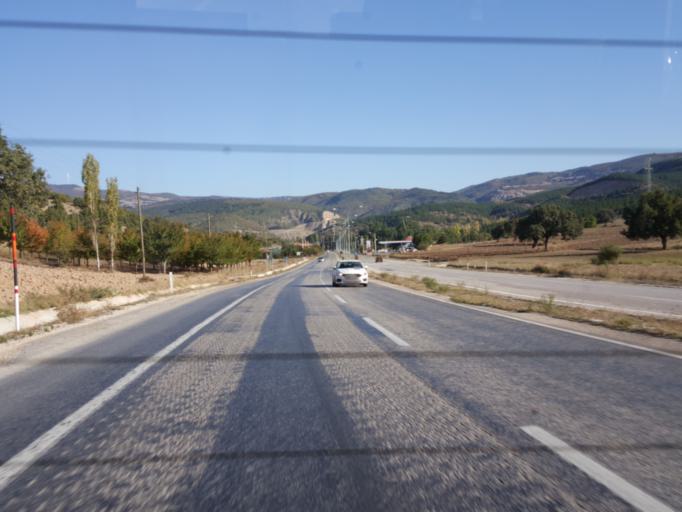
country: TR
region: Amasya
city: Ezinepazari
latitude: 40.5601
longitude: 36.1384
